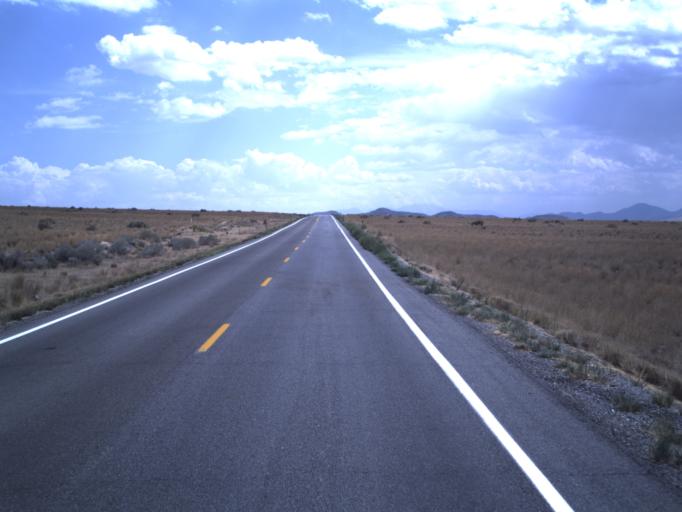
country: US
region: Utah
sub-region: Utah County
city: Eagle Mountain
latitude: 40.2687
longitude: -112.2420
